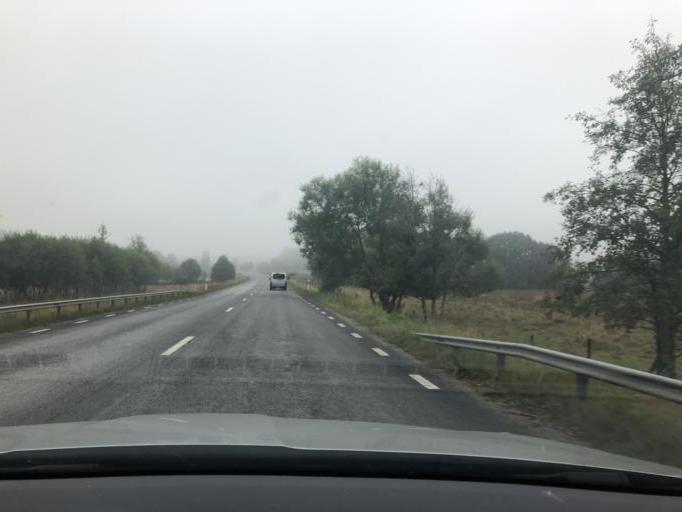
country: SE
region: Uppsala
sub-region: Tierps Kommun
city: Tierp
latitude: 60.3266
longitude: 17.5162
